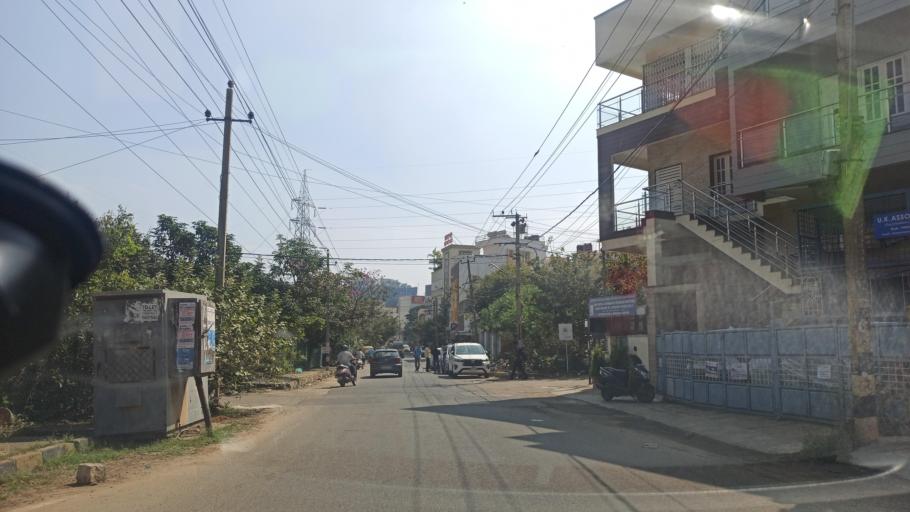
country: IN
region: Karnataka
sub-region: Bangalore Urban
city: Yelahanka
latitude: 13.0597
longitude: 77.5897
